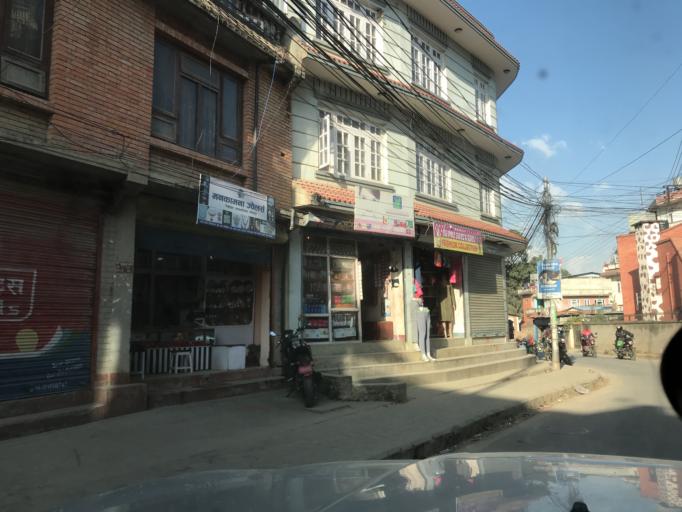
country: NP
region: Central Region
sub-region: Bagmati Zone
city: Patan
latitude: 27.6604
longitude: 85.3175
